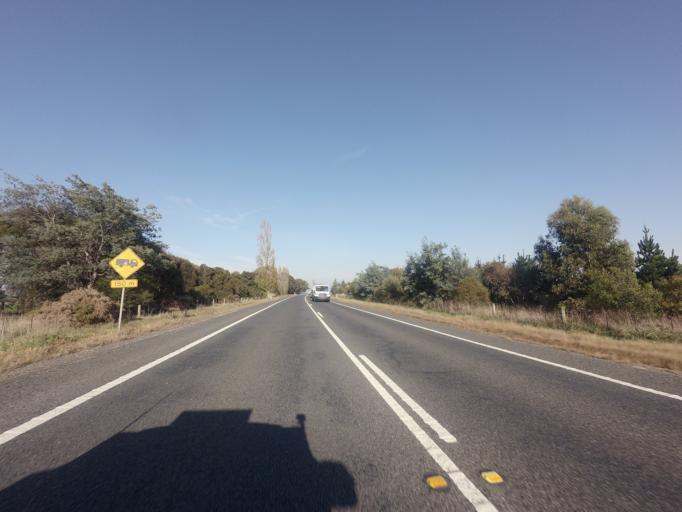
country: AU
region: Tasmania
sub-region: Northern Midlands
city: Longford
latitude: -41.5803
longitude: 147.1357
